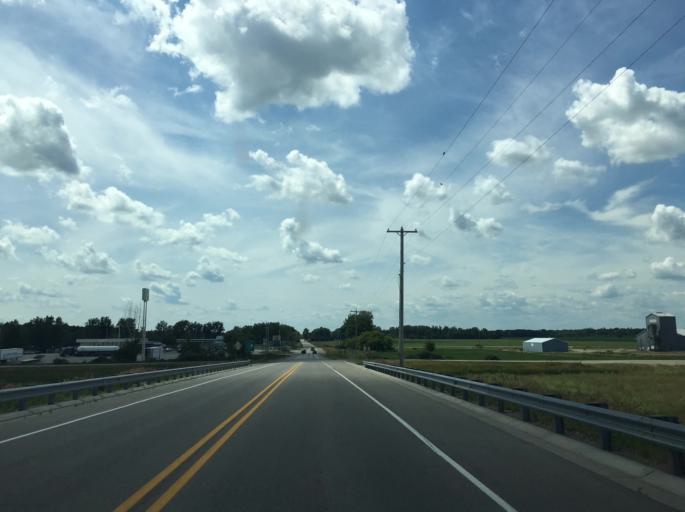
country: US
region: Michigan
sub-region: Bay County
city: Pinconning
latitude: 43.8540
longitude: -84.0215
